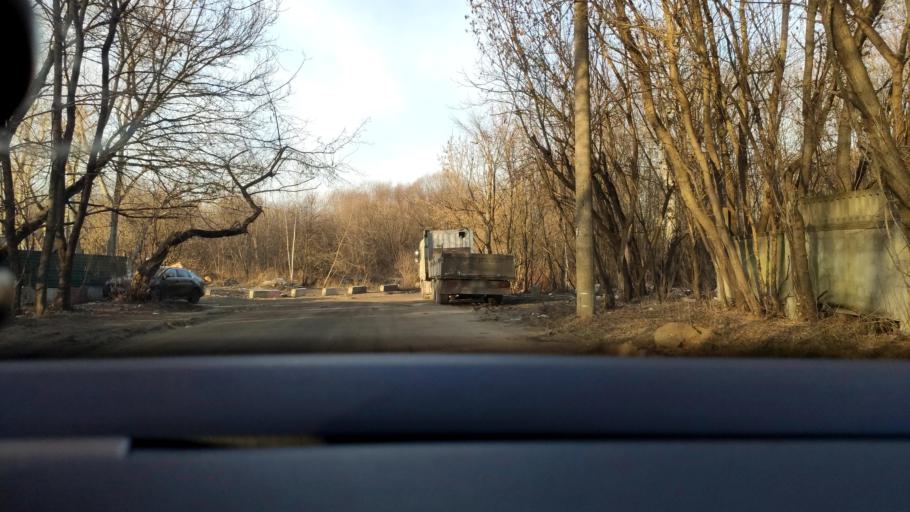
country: RU
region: Moskovskaya
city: Fili
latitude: 55.7499
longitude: 37.4597
